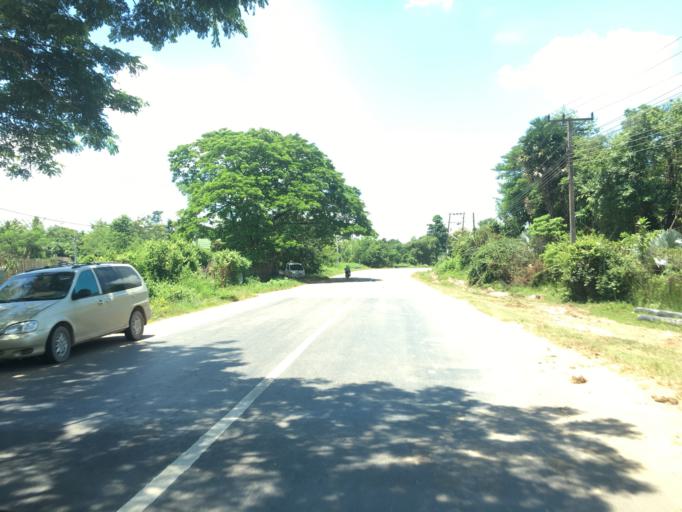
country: LA
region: Vientiane
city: Muang Phon-Hong
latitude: 18.2384
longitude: 102.4848
